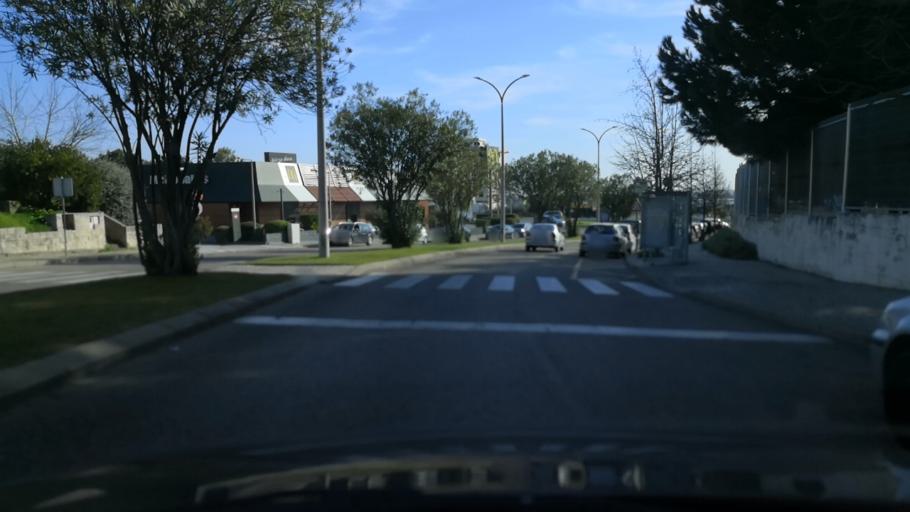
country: PT
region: Santarem
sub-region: Torres Novas
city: Torres Novas
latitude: 39.4721
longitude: -8.5404
